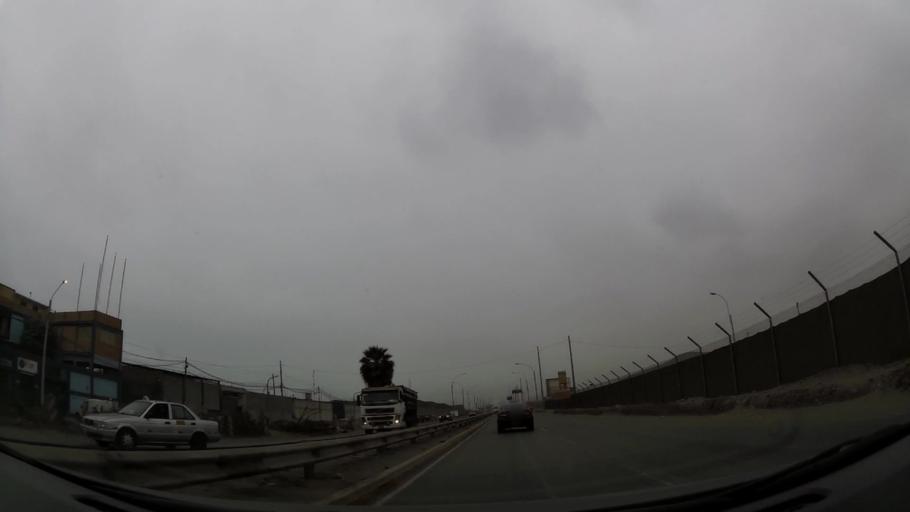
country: PE
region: Callao
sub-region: Callao
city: Callao
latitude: -12.0028
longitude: -77.1269
